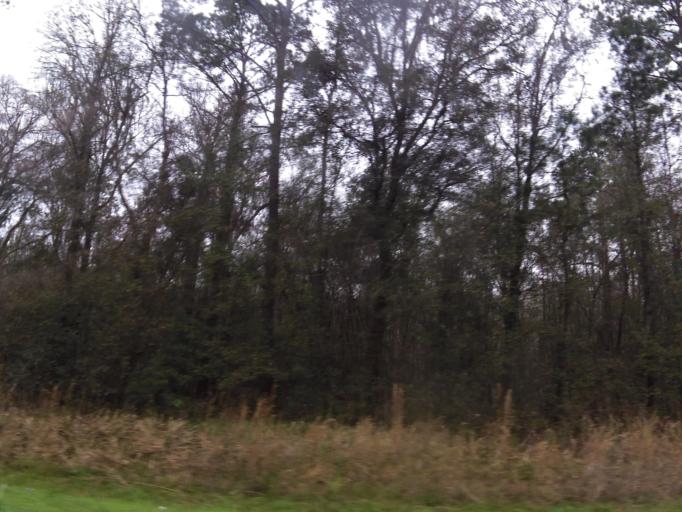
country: US
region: Florida
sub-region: Union County
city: Lake Butler
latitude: 29.9150
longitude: -82.4271
